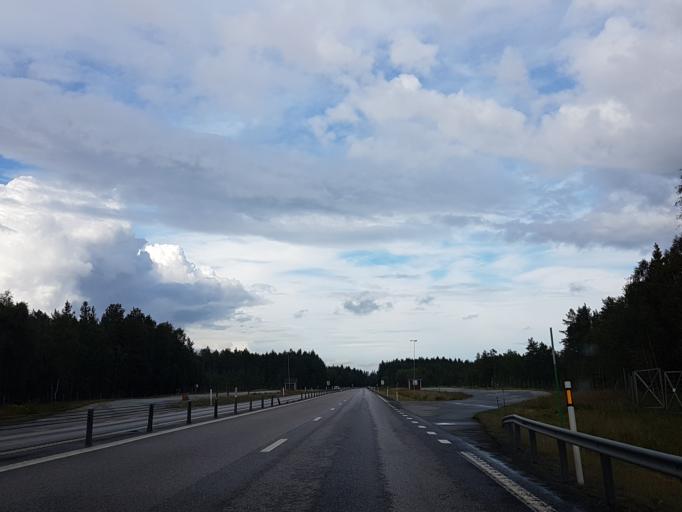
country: SE
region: Vaesterbotten
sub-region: Umea Kommun
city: Saevar
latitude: 63.9107
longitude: 20.5894
